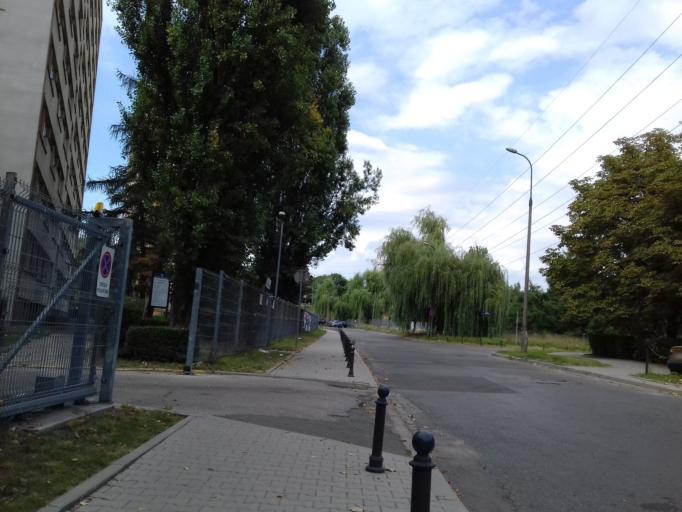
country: PL
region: Lesser Poland Voivodeship
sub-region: Krakow
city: Krakow
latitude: 50.0850
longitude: 19.9971
